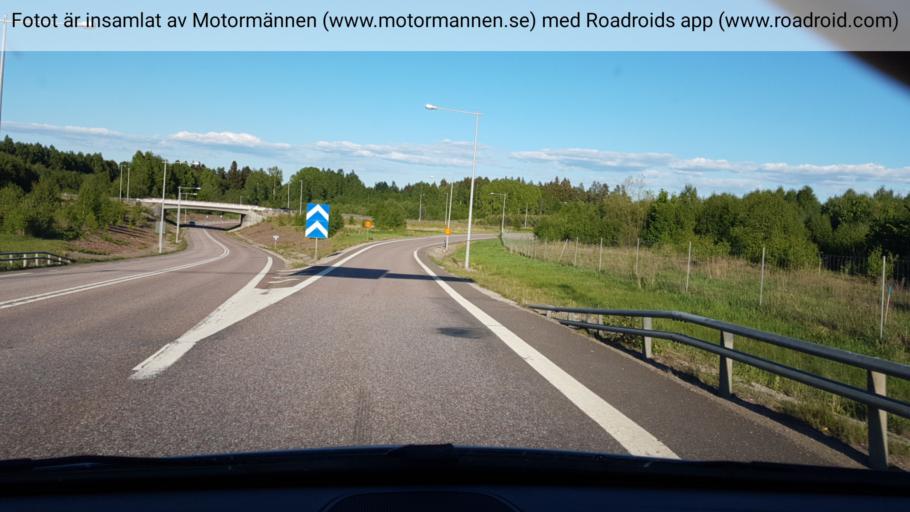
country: SE
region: Vaestra Goetaland
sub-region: Skovde Kommun
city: Skoevde
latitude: 58.3677
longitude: 13.8511
